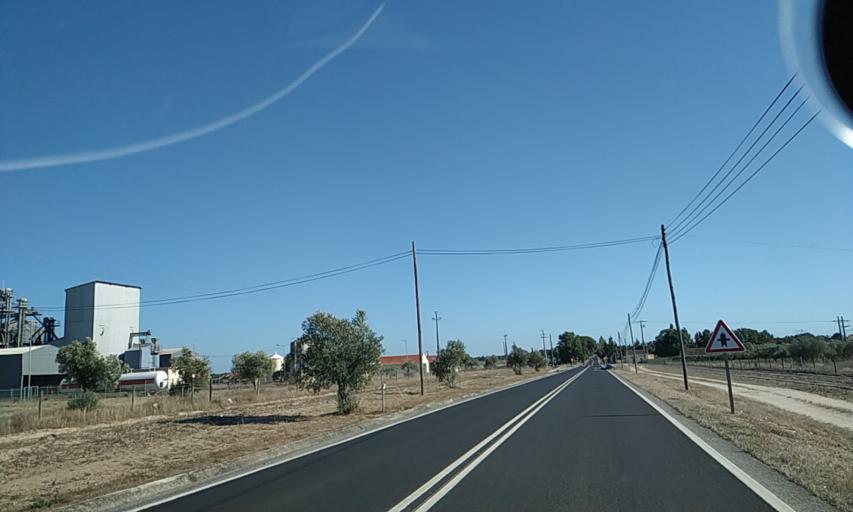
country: PT
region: Santarem
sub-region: Benavente
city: Poceirao
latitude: 38.8157
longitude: -8.8809
